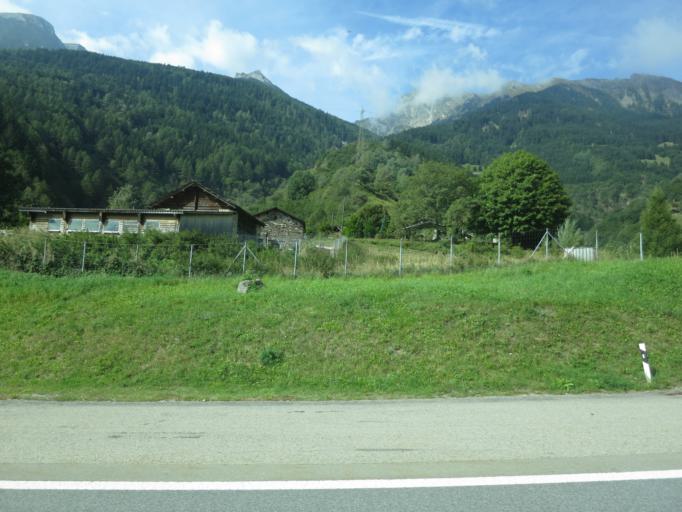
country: CH
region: Grisons
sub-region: Moesa District
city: Mesocco
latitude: 46.3995
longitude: 9.2291
